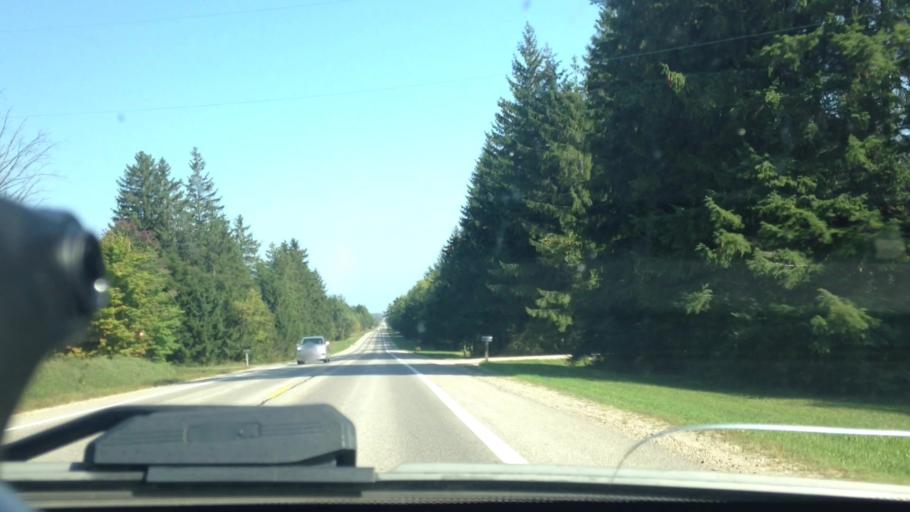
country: US
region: Michigan
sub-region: Luce County
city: Newberry
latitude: 46.3037
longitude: -85.4335
